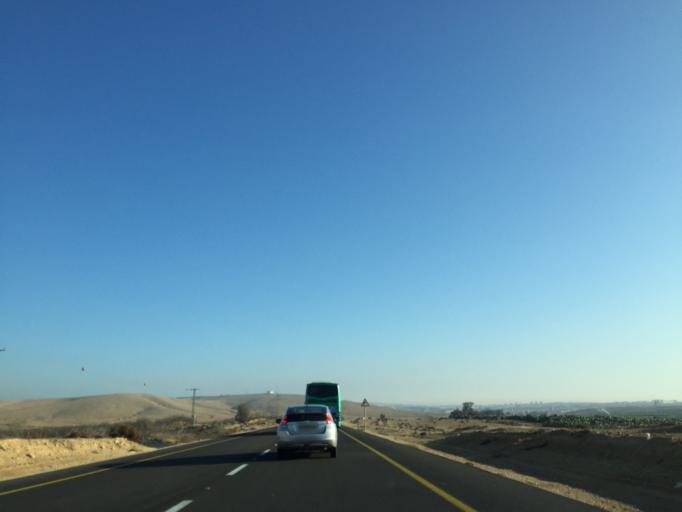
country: IL
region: Southern District
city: Dimona
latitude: 31.0445
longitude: 34.9814
